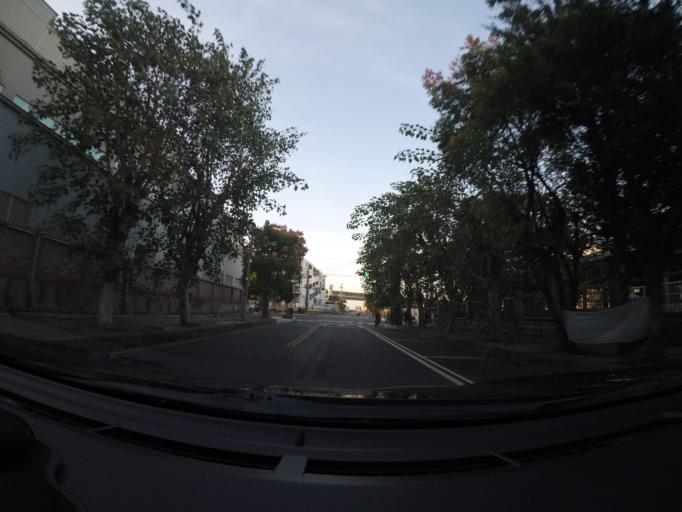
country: TW
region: Taiwan
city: Taoyuan City
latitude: 24.9928
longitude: 121.2457
